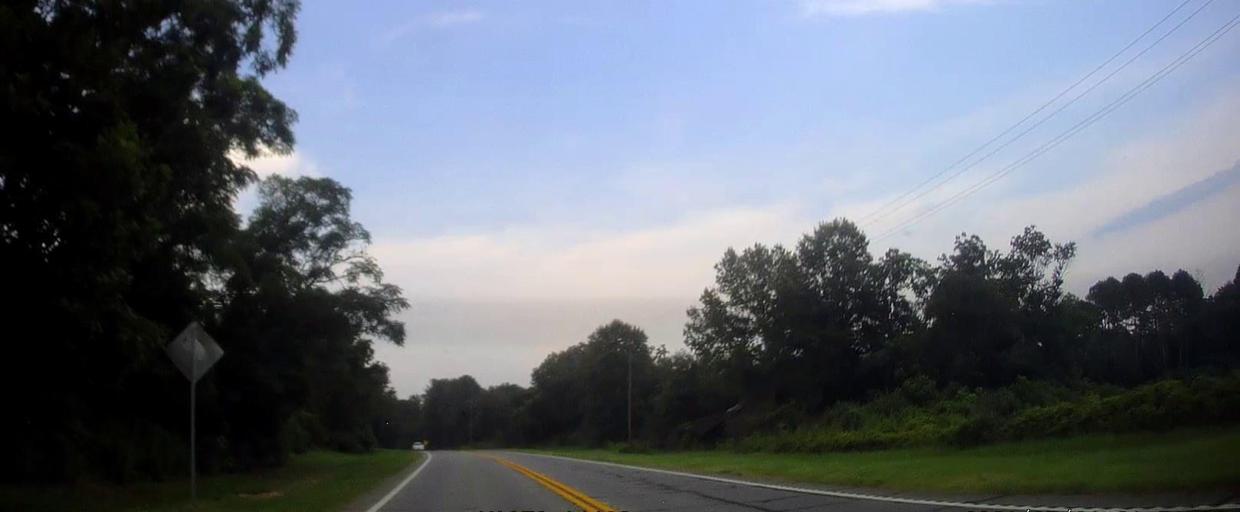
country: US
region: Georgia
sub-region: Laurens County
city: East Dublin
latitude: 32.5693
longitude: -82.8425
